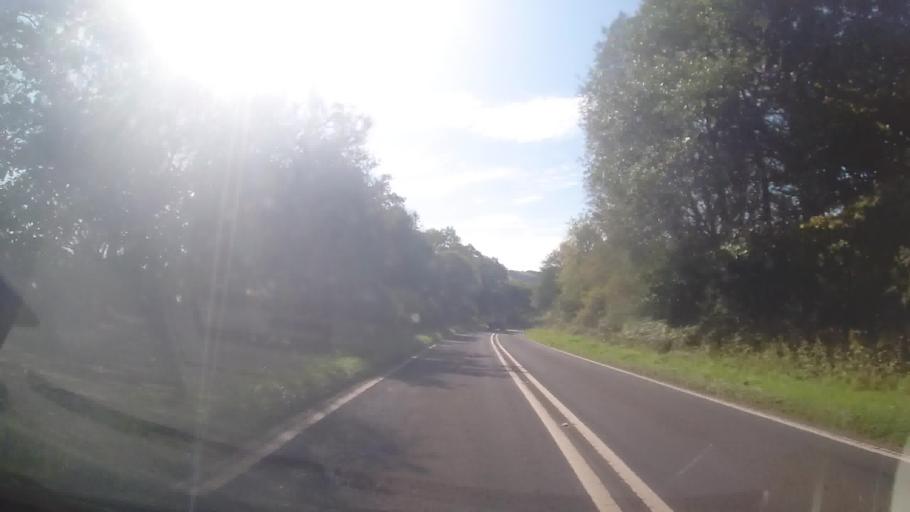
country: GB
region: Wales
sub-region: Sir Powys
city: Llandrindod Wells
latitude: 52.2821
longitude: -3.3904
